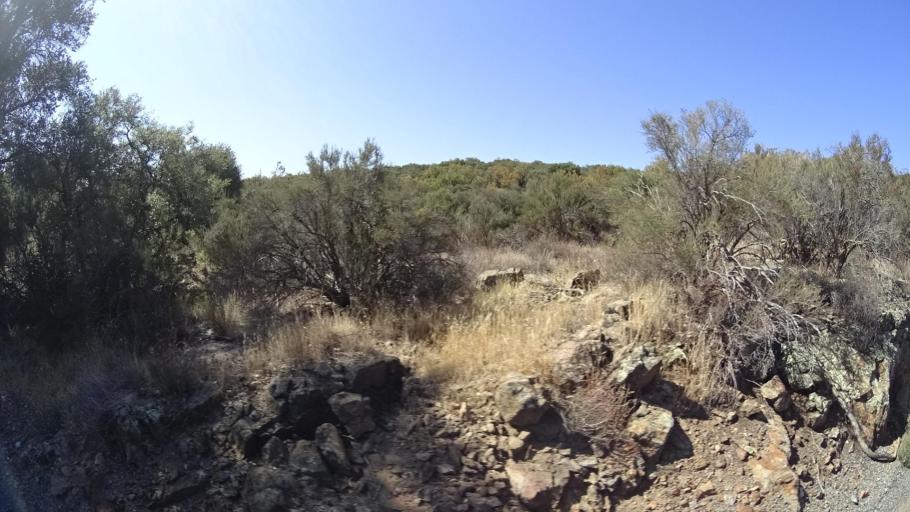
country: US
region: California
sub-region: Riverside County
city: Aguanga
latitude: 33.3184
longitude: -116.6969
